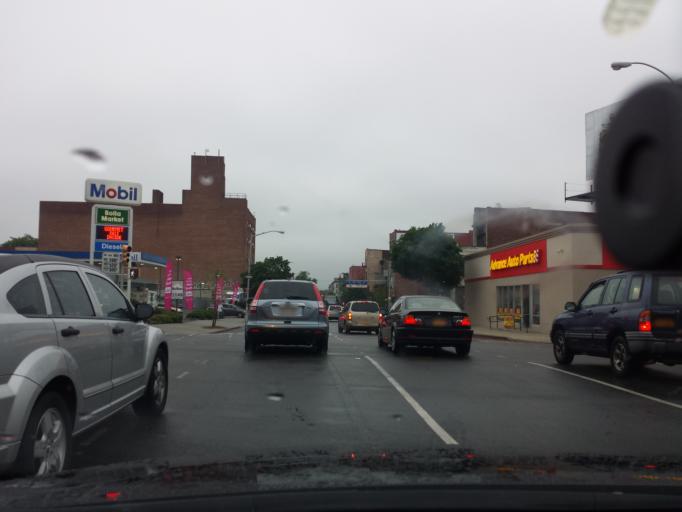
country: US
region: New York
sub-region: Kings County
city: Brooklyn
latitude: 40.6786
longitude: -73.9530
